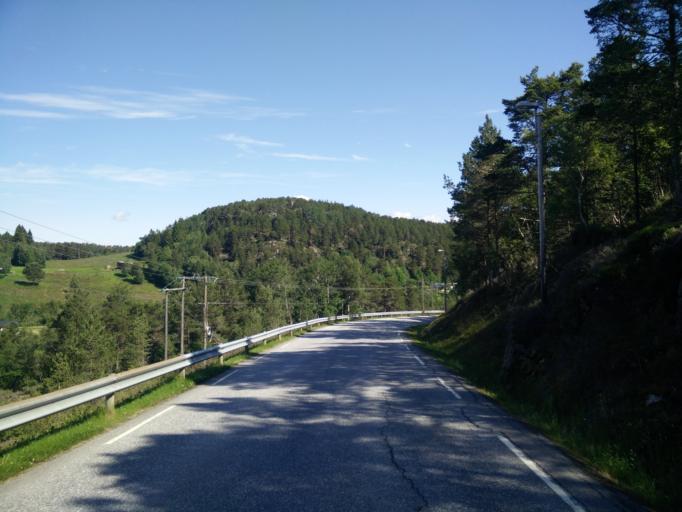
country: NO
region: More og Romsdal
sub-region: Kristiansund
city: Rensvik
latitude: 63.0675
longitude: 7.8713
